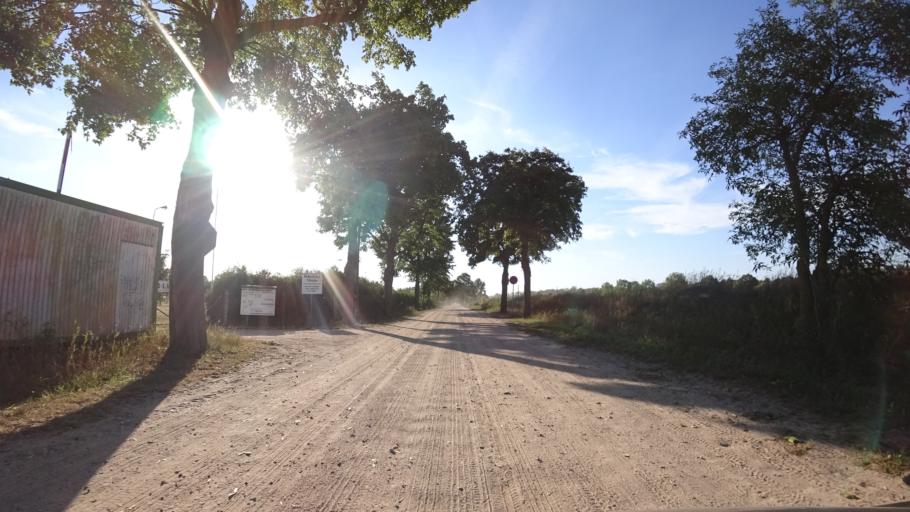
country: DE
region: Brandenburg
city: Stahnsdorf
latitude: 52.3441
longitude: 13.1799
